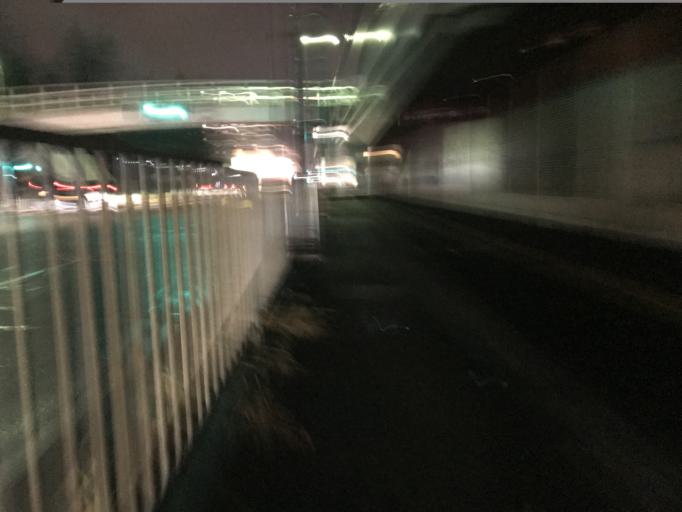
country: JP
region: Shiga Prefecture
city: Otsu-shi
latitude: 35.0191
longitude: 135.8611
